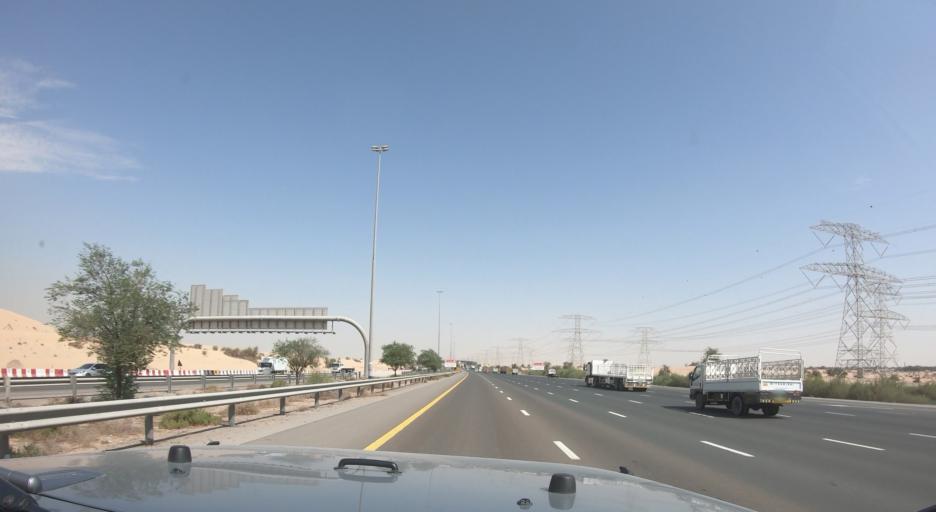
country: AE
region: Ash Shariqah
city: Sharjah
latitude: 25.1732
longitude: 55.5088
